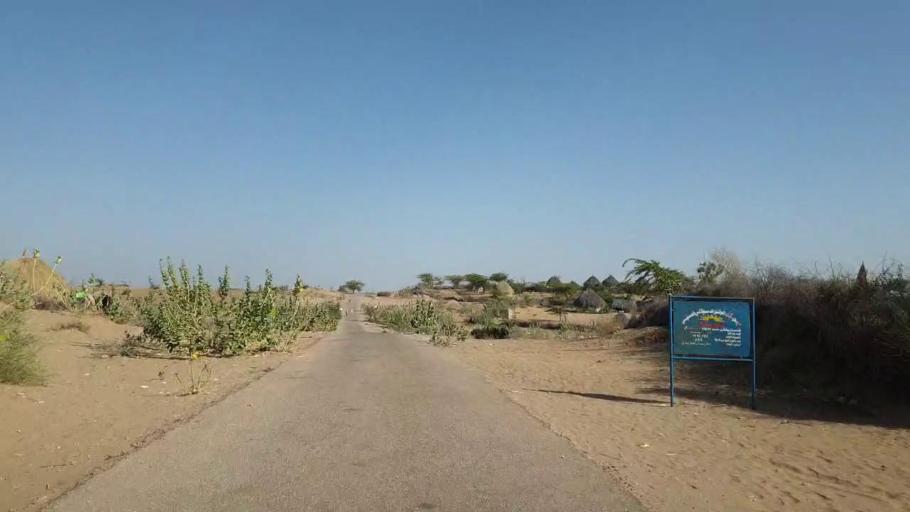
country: PK
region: Sindh
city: Islamkot
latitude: 25.0396
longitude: 70.0196
